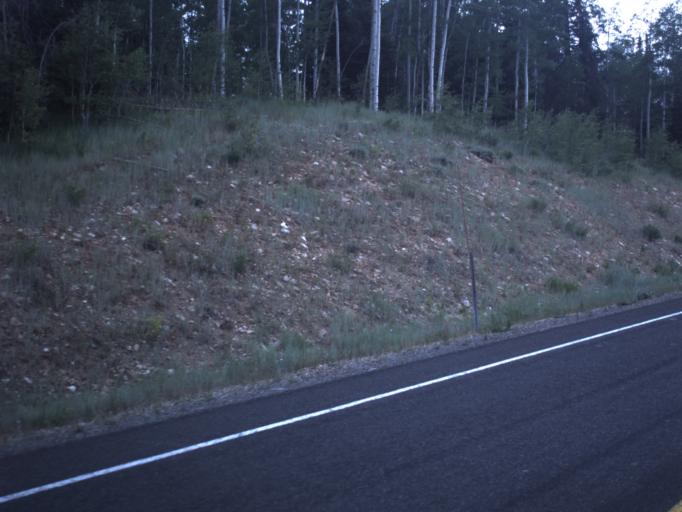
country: US
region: Utah
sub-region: Summit County
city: Francis
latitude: 40.4894
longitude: -110.9631
